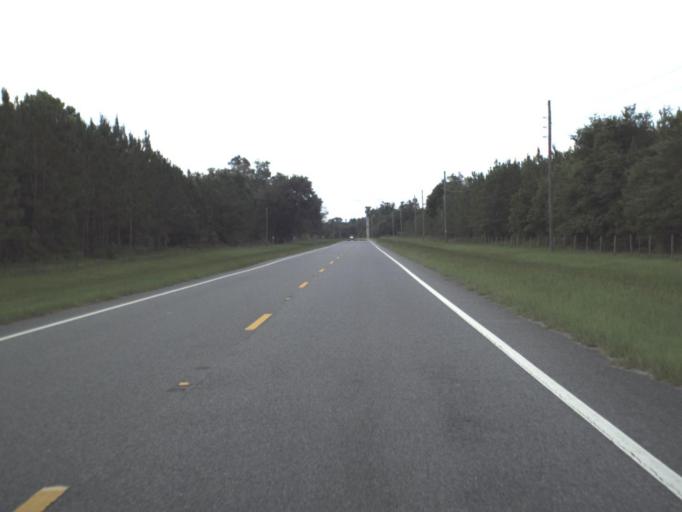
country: US
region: Florida
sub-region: Clay County
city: Asbury Lake
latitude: 29.9778
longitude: -81.8660
